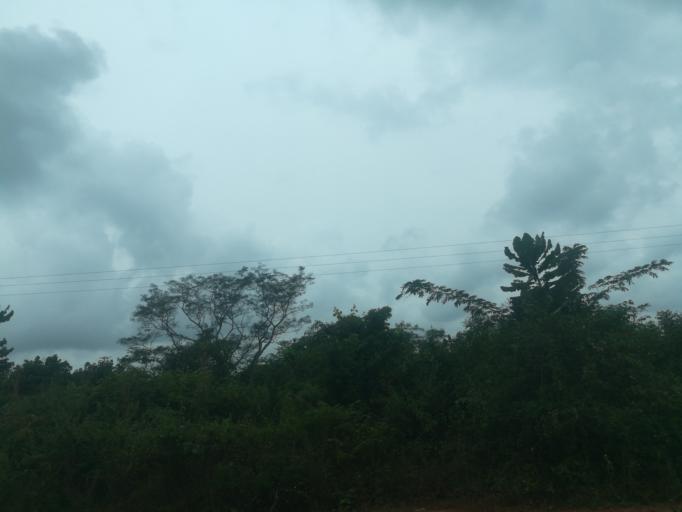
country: NG
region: Ogun
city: Ayetoro
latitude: 7.1056
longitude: 3.1461
